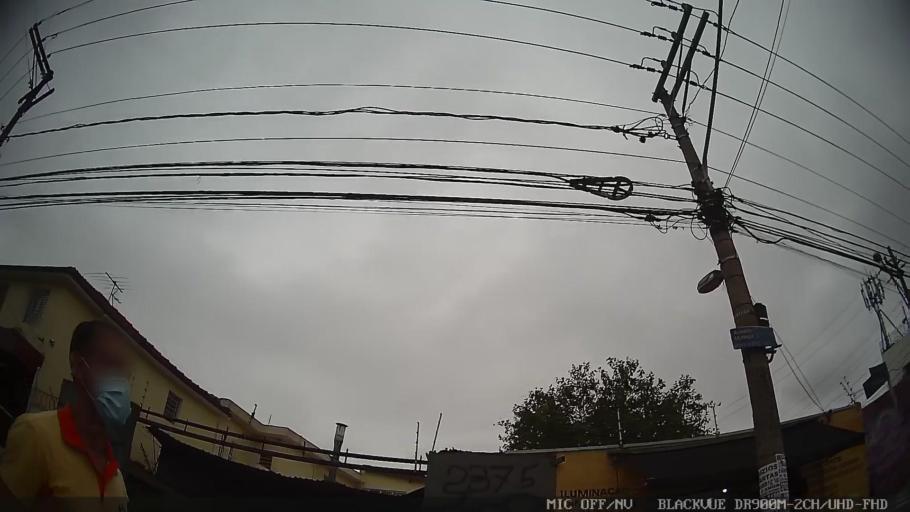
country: BR
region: Sao Paulo
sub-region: Osasco
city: Osasco
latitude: -23.4867
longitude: -46.7475
